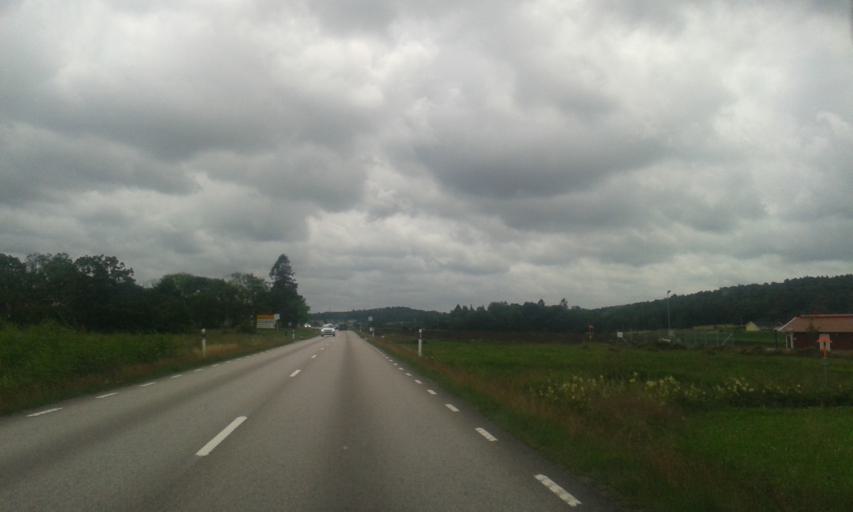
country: SE
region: Vaestra Goetaland
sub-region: Kungalvs Kommun
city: Kode
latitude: 57.8819
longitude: 11.8935
